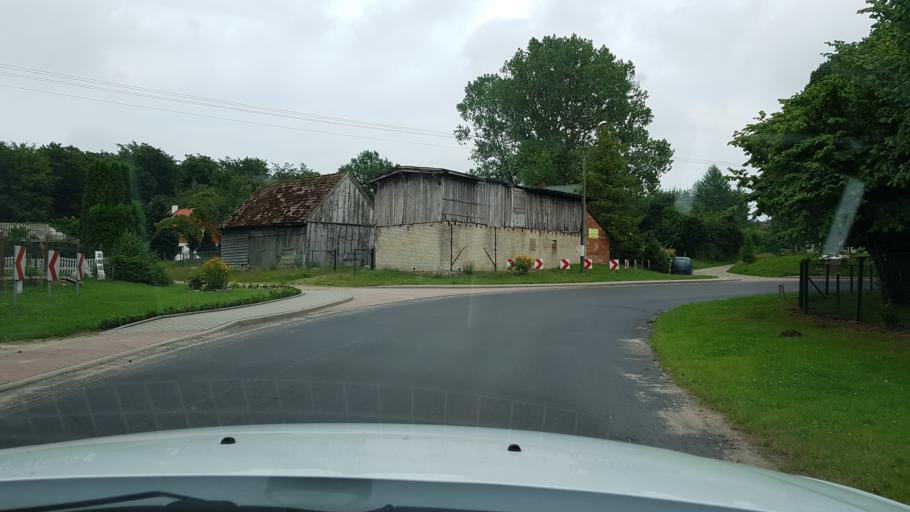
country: PL
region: West Pomeranian Voivodeship
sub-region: Powiat slawienski
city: Slawno
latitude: 54.4879
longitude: 16.5833
